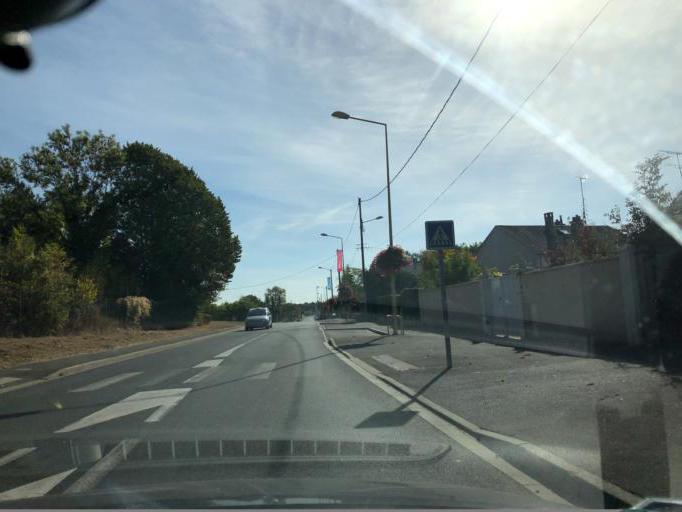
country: FR
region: Centre
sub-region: Departement du Loiret
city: Malesherbes
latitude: 48.2965
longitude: 2.3916
